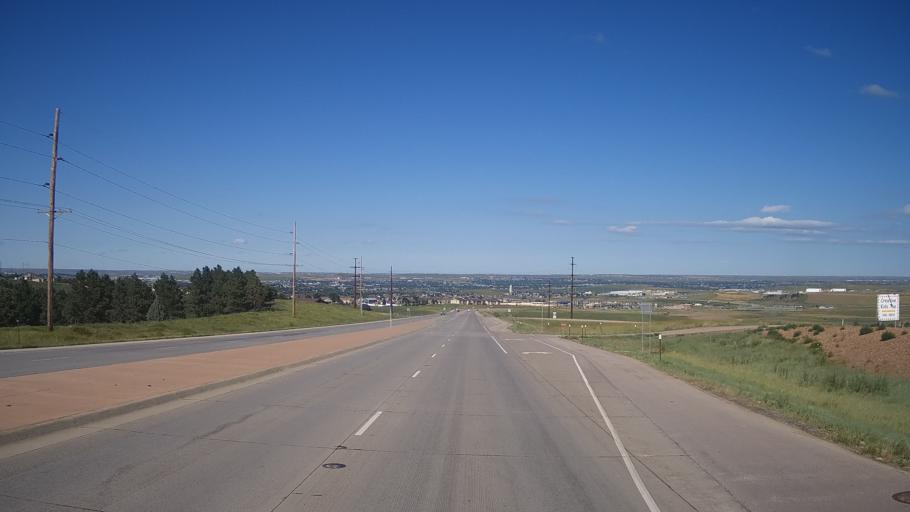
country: US
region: South Dakota
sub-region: Pennington County
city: Rapid City
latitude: 44.0254
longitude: -103.2354
